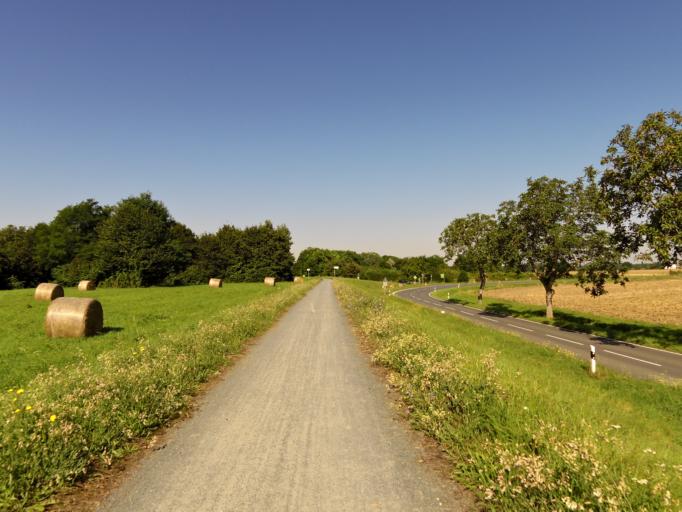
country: DE
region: Hesse
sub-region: Regierungsbezirk Darmstadt
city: Stockstadt am Rhein
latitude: 49.8398
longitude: 8.4443
